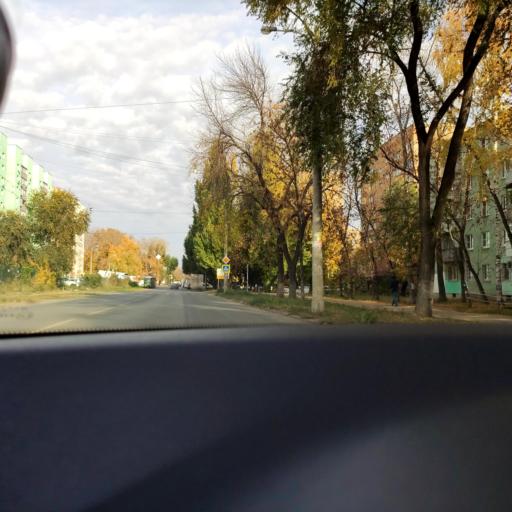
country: RU
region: Samara
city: Samara
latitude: 53.2330
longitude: 50.2566
